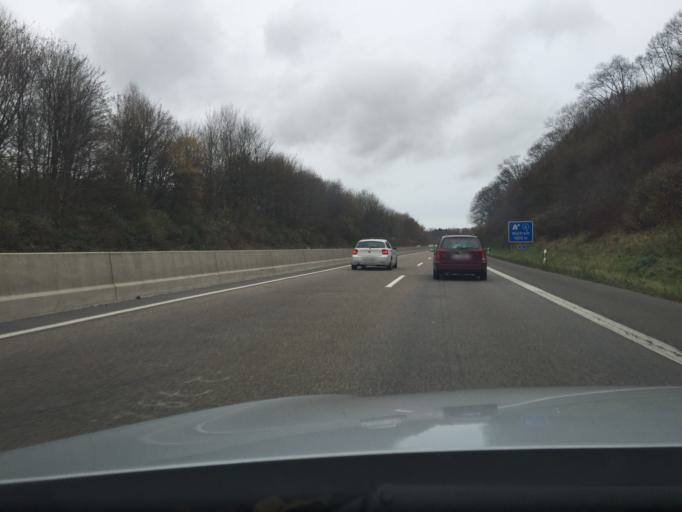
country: DE
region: North Rhine-Westphalia
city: Wulfrath
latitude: 51.2857
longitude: 7.0722
